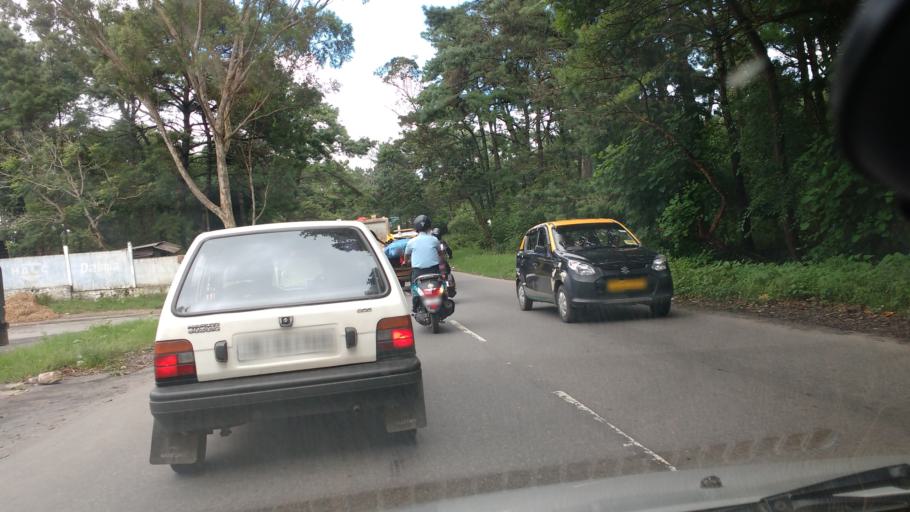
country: IN
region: Meghalaya
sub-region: East Khasi Hills
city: Shillong
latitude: 25.5538
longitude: 91.8455
